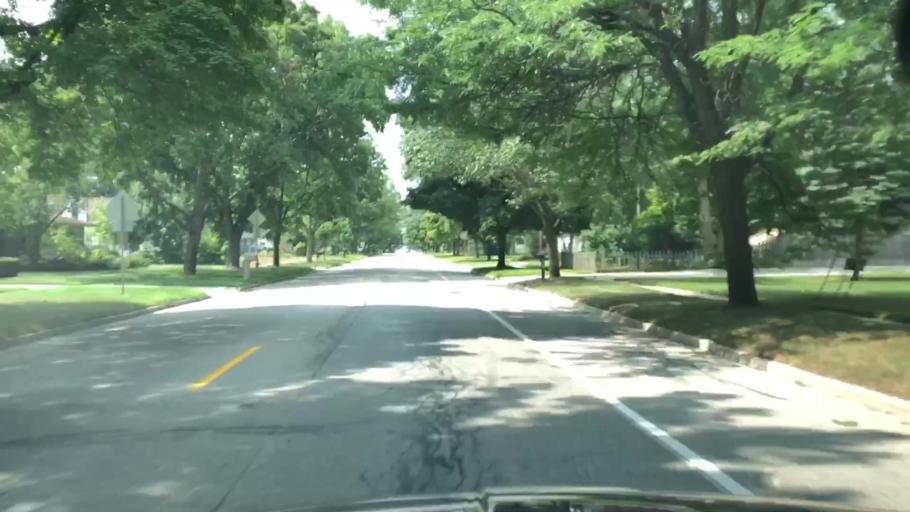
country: US
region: Michigan
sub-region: Midland County
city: Midland
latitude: 43.6266
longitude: -84.1983
